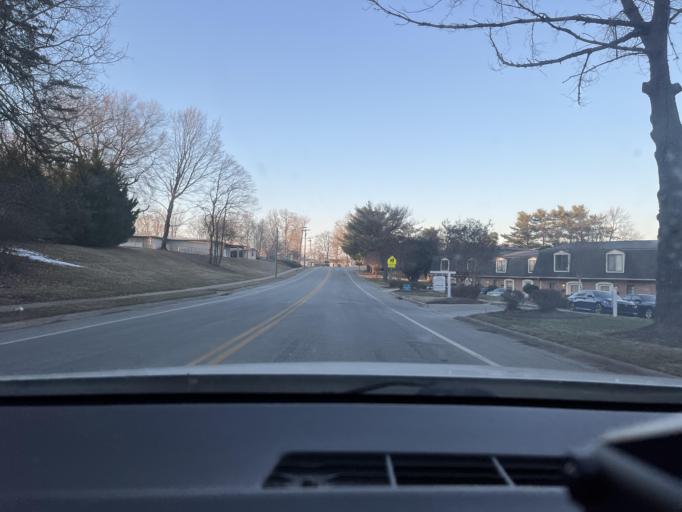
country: US
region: North Carolina
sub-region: Guilford County
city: Greensboro
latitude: 36.0299
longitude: -79.8298
